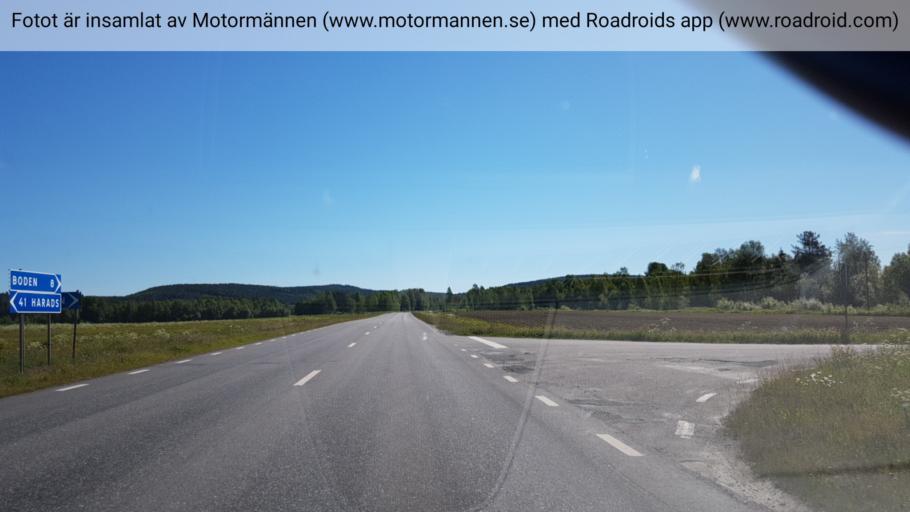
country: SE
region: Norrbotten
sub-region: Bodens Kommun
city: Boden
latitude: 65.8511
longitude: 21.5592
